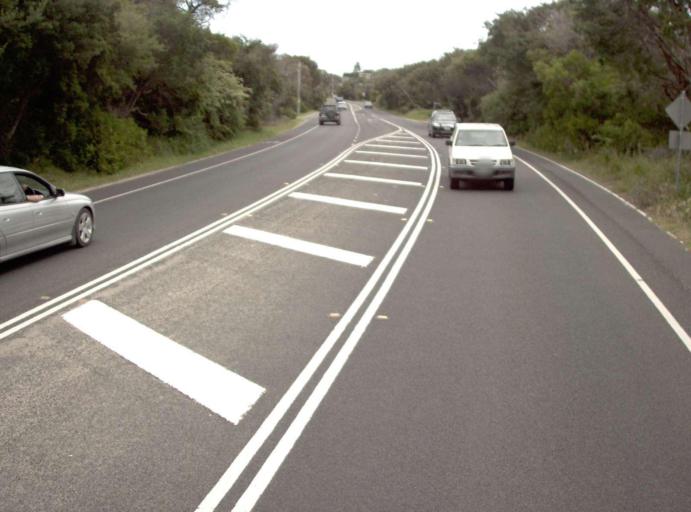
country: AU
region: Victoria
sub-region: Mornington Peninsula
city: Blairgowrie
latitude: -38.3547
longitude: 144.7630
